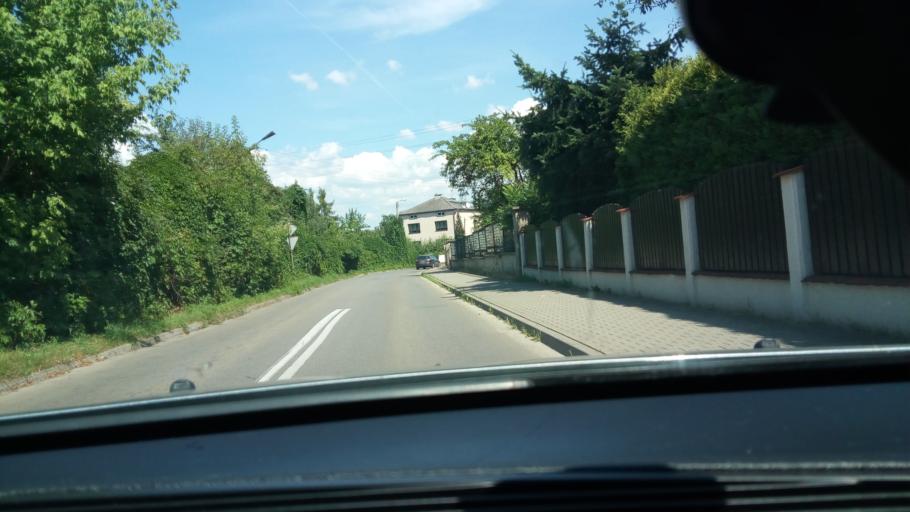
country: PL
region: Lesser Poland Voivodeship
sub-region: Powiat chrzanowski
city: Chrzanow
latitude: 50.1352
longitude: 19.4095
